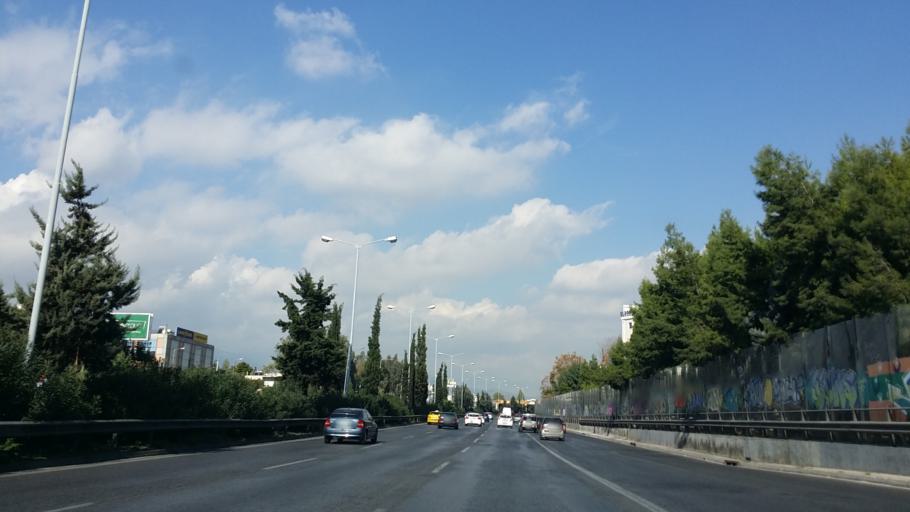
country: GR
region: Attica
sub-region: Nomarchia Athinas
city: Nea Chalkidona
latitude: 38.0270
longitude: 23.7272
